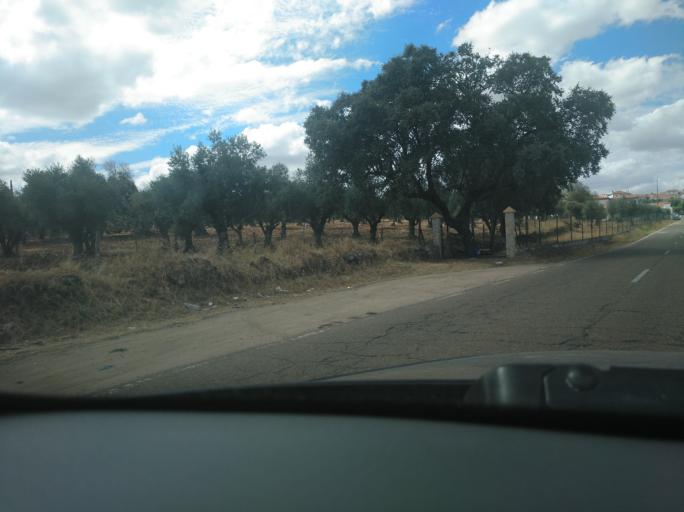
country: PT
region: Portalegre
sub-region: Arronches
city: Arronches
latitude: 39.0489
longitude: -7.4342
